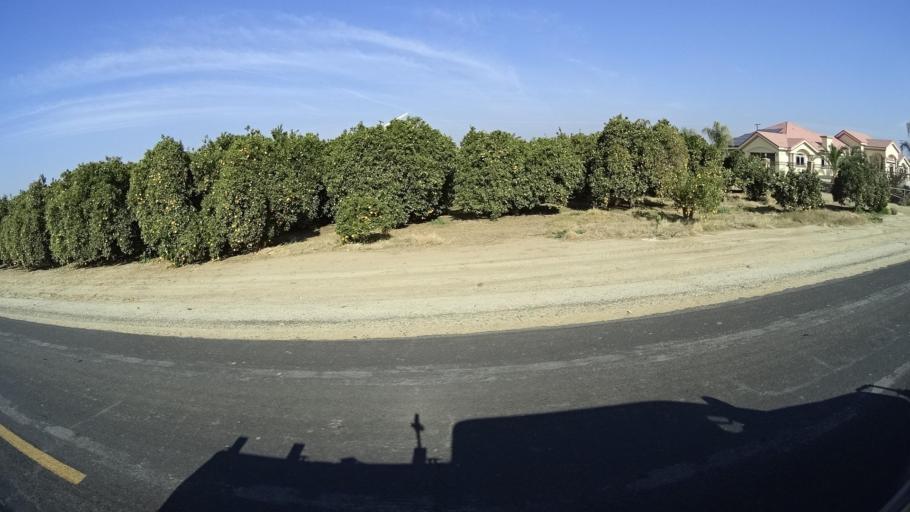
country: US
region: California
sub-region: Kern County
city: McFarland
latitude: 35.6746
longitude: -119.1549
